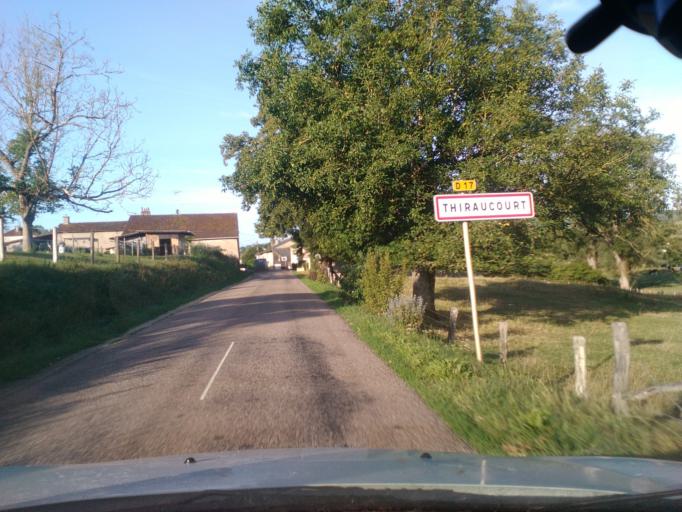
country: FR
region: Lorraine
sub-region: Departement des Vosges
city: Mirecourt
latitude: 48.2942
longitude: 6.0754
